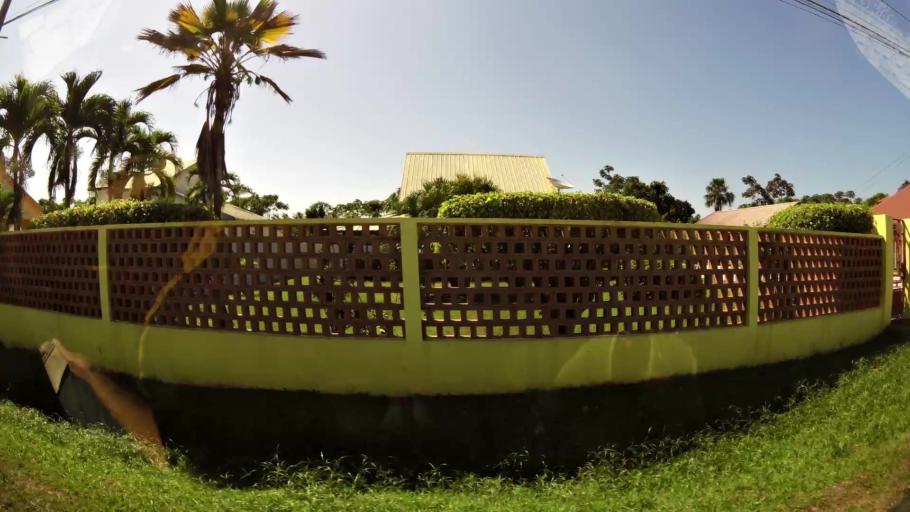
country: GF
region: Guyane
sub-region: Guyane
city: Remire-Montjoly
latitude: 4.9235
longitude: -52.2816
